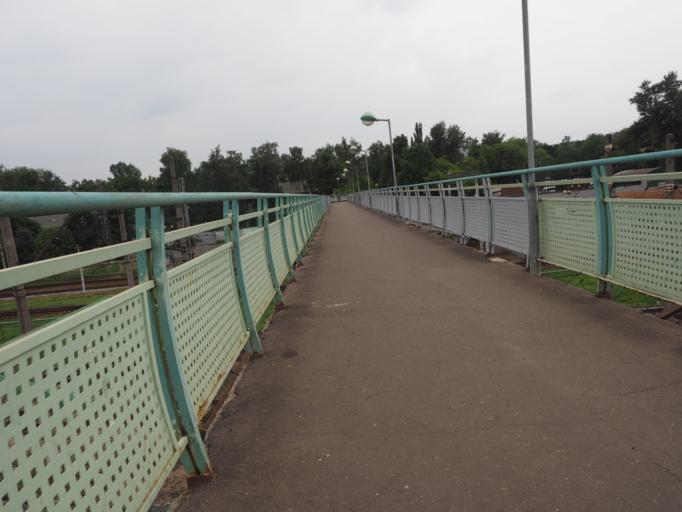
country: RU
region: Moskovskaya
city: Tomilino
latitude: 55.6685
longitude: 37.9249
